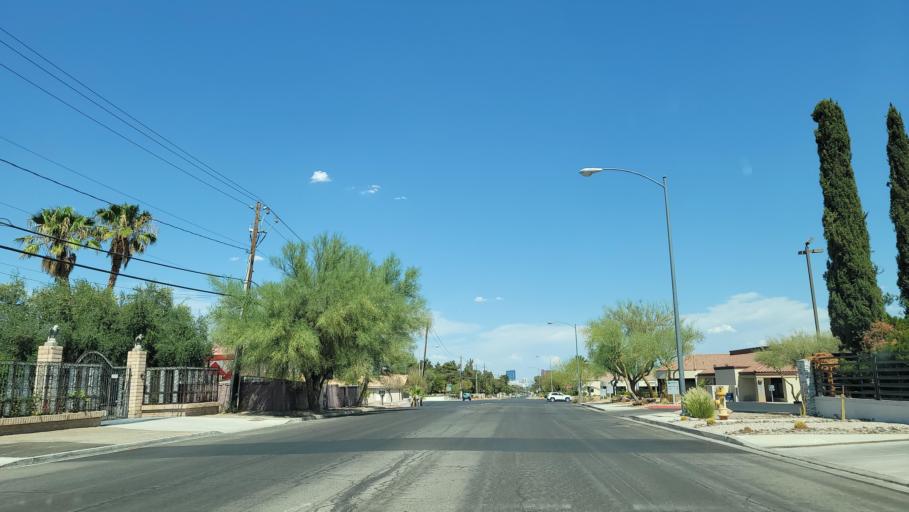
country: US
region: Nevada
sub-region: Clark County
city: Spring Valley
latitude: 36.1368
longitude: -115.2445
